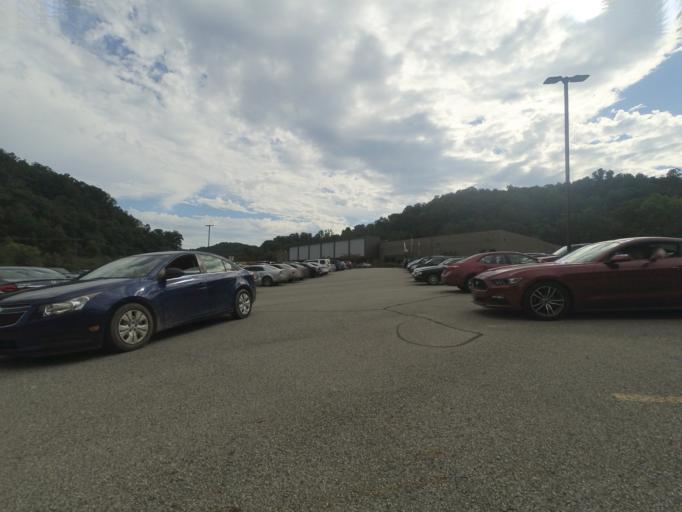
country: US
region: West Virginia
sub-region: Cabell County
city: Huntington
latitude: 38.3895
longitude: -82.4565
